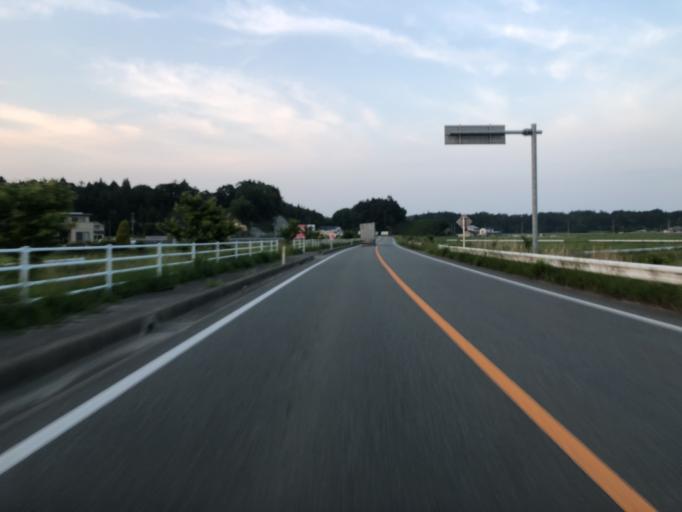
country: JP
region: Fukushima
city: Namie
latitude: 37.5246
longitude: 140.9991
